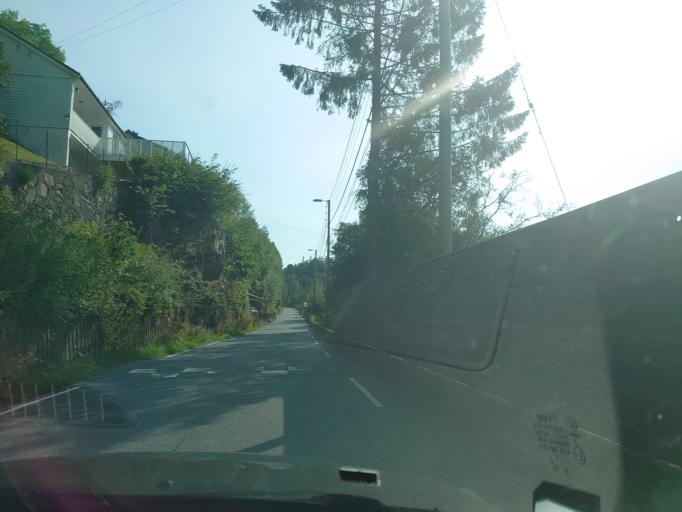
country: NO
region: Hordaland
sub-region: Bergen
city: Ytrebygda
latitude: 60.3303
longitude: 5.2825
